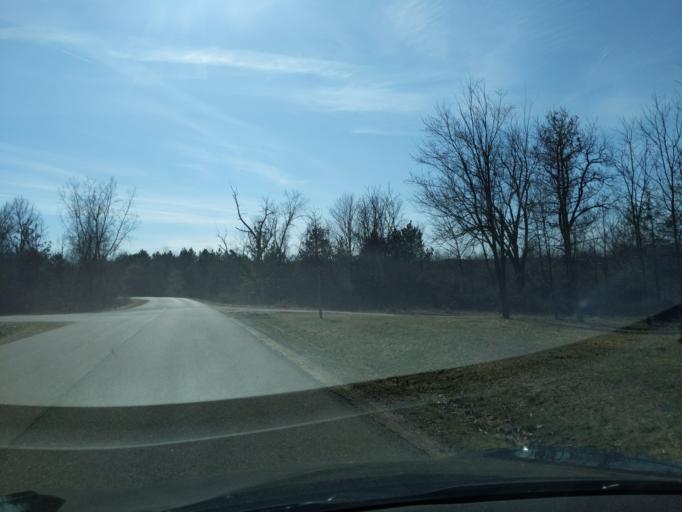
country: US
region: Michigan
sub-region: Ionia County
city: Ionia
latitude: 42.9464
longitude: -85.1334
